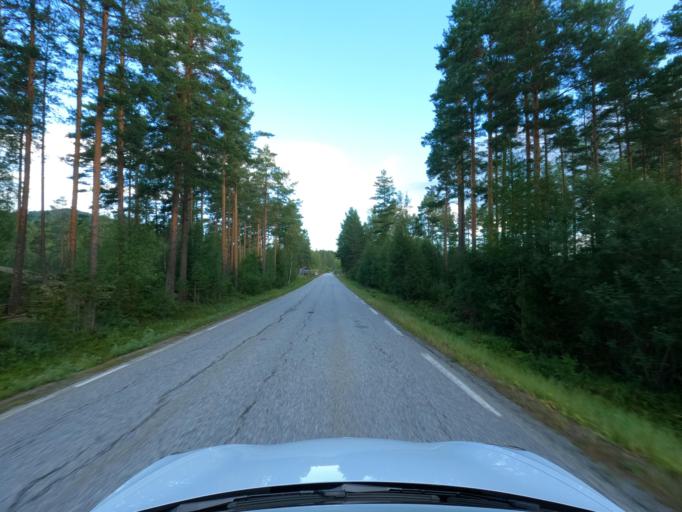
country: NO
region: Telemark
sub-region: Hjartdal
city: Sauland
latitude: 59.8017
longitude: 9.0861
